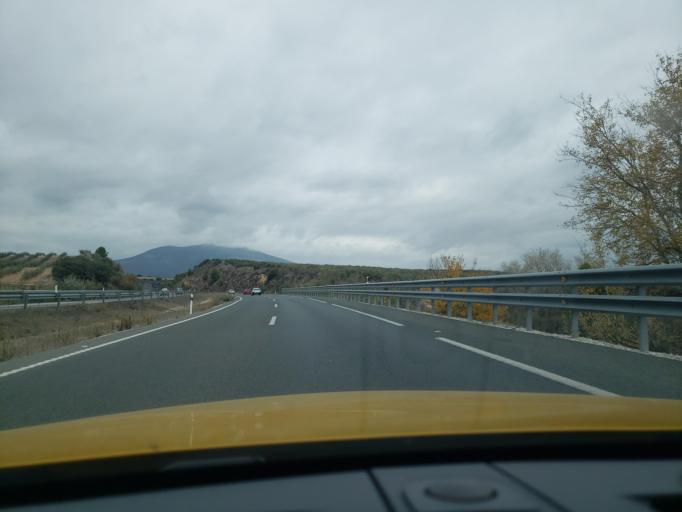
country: ES
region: Andalusia
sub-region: Provincia de Granada
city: Calicasas
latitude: 37.2939
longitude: -3.6564
